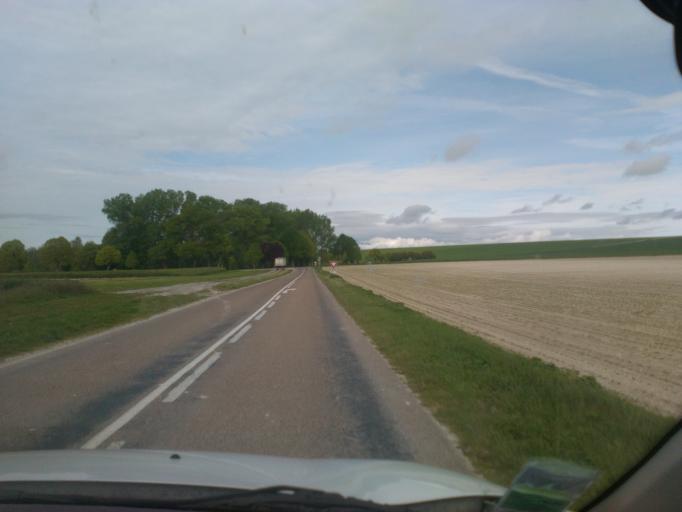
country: FR
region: Champagne-Ardenne
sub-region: Departement de l'Aube
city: Marigny-le-Chatel
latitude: 48.3618
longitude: 3.7136
